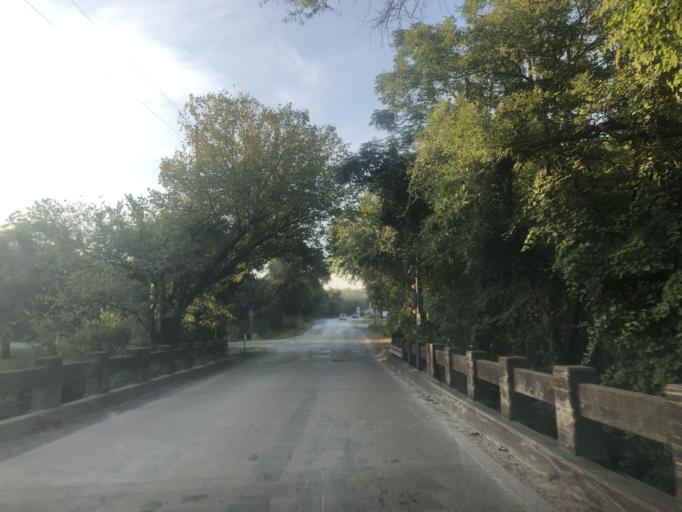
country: US
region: Texas
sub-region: Tarrant County
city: Lakeside
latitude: 32.7929
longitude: -97.4929
